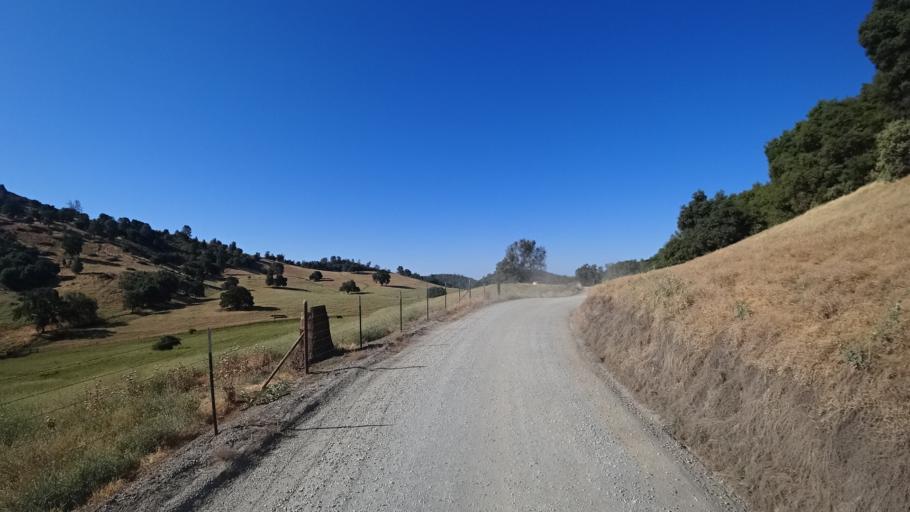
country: US
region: California
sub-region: Calaveras County
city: Angels Camp
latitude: 38.0692
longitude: -120.4956
